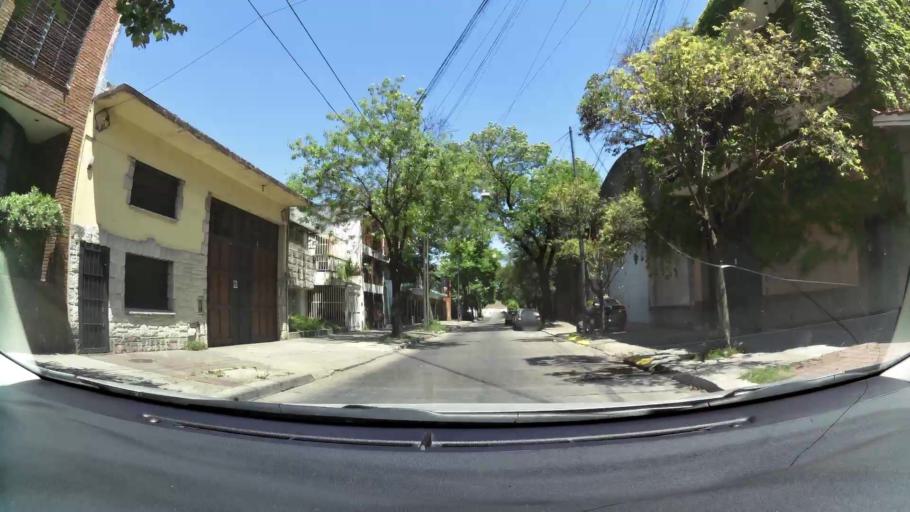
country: AR
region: Buenos Aires
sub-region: Partido de Avellaneda
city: Avellaneda
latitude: -34.6501
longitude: -58.3915
